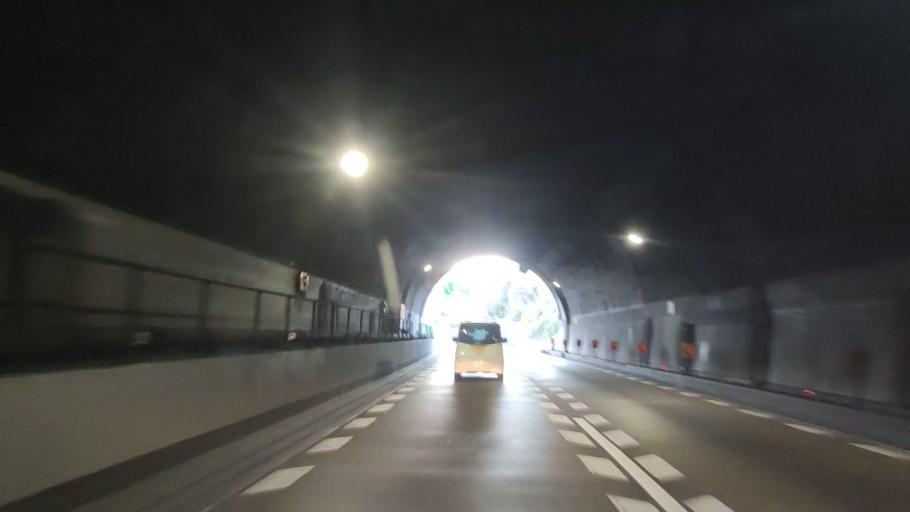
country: JP
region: Hyogo
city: Tatsunocho-tominaga
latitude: 34.8372
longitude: 134.6150
